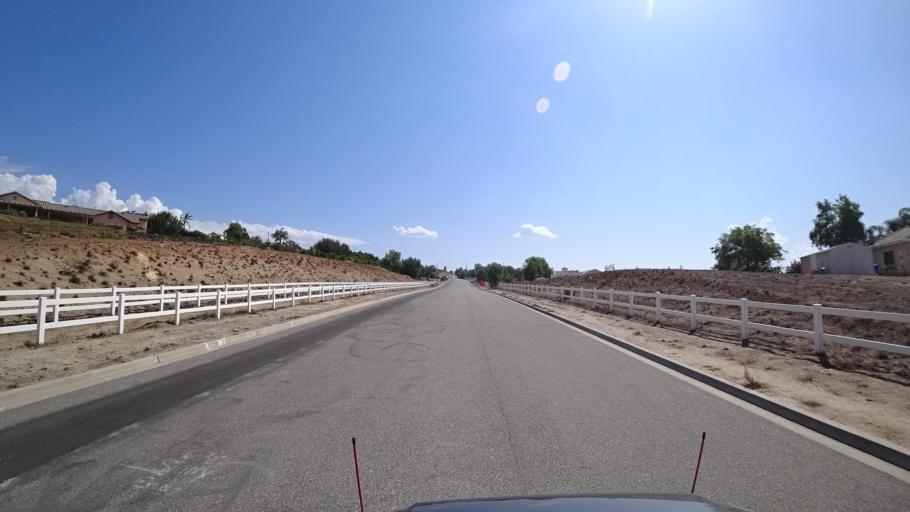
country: US
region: California
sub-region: San Diego County
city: Valley Center
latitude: 33.2820
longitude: -117.0129
